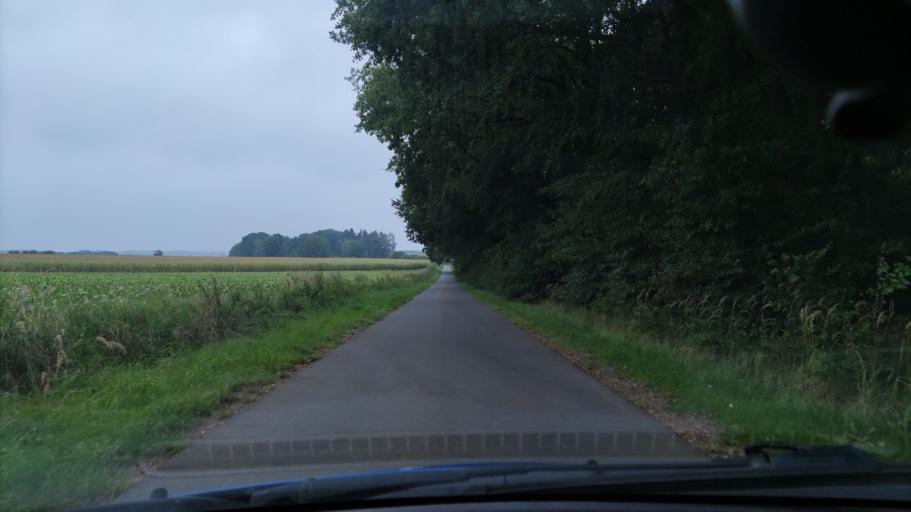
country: DE
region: Lower Saxony
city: Emmendorf
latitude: 53.0273
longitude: 10.5951
